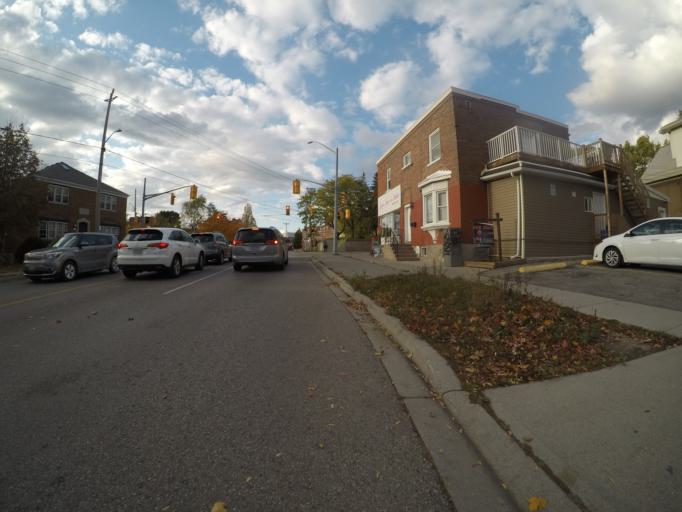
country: CA
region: Ontario
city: Waterloo
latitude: 43.4541
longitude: -80.5101
